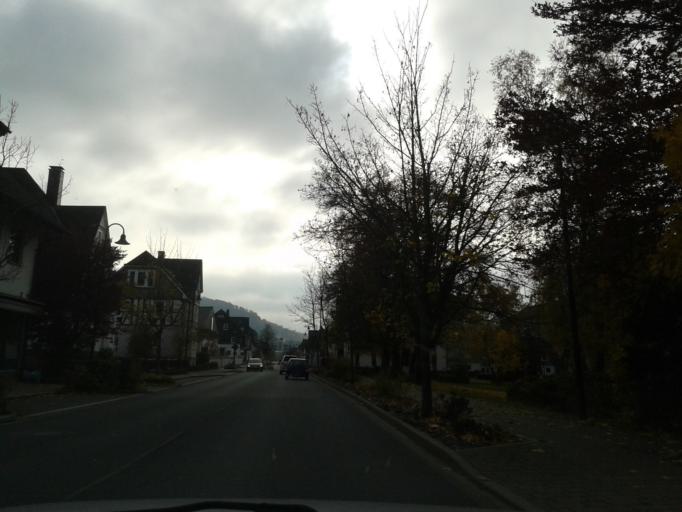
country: DE
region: North Rhine-Westphalia
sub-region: Regierungsbezirk Arnsberg
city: Bad Berleburg
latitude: 51.0555
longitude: 8.3936
